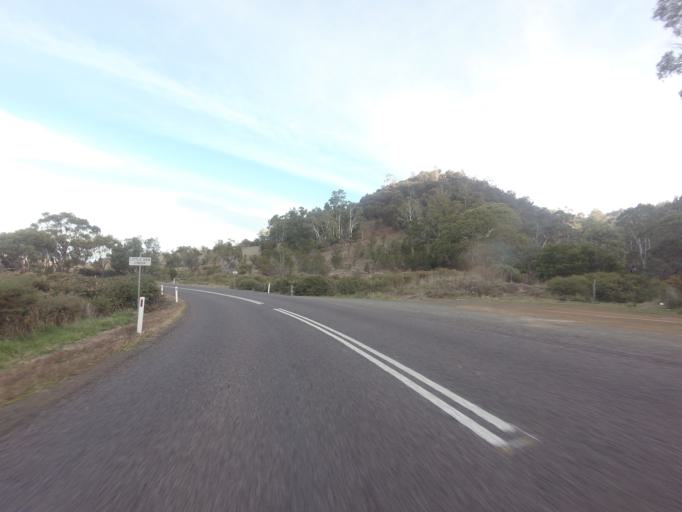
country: AU
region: Tasmania
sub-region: Brighton
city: Bridgewater
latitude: -42.4248
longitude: 147.1387
